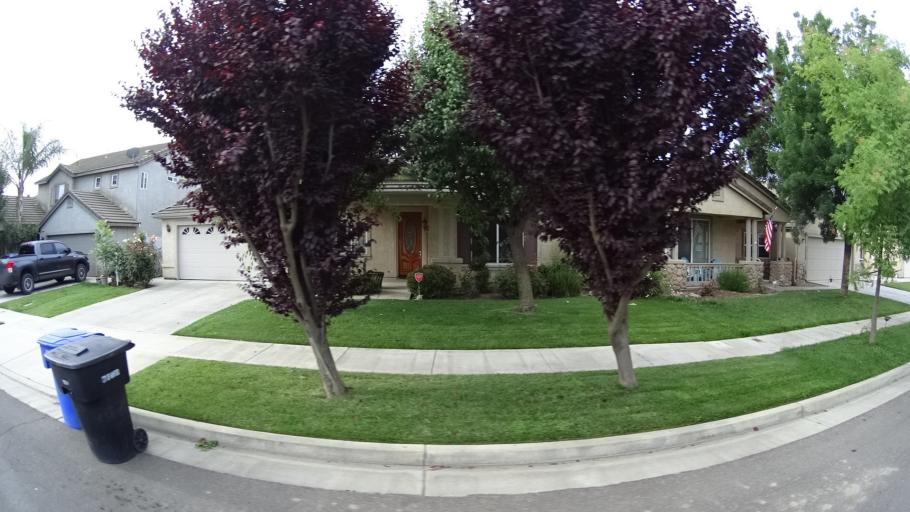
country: US
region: California
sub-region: Kings County
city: Hanford
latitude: 36.3341
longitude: -119.6775
